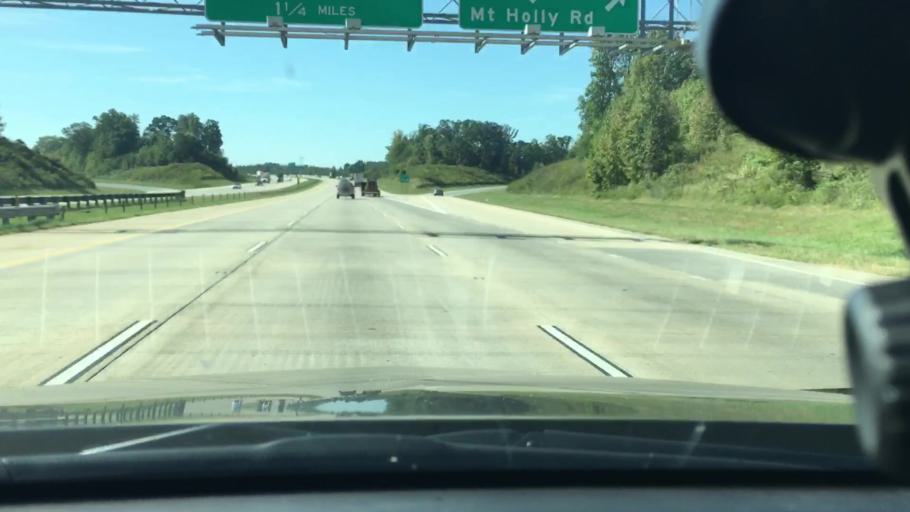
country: US
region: North Carolina
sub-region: Gaston County
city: Mount Holly
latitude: 35.2948
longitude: -80.9605
